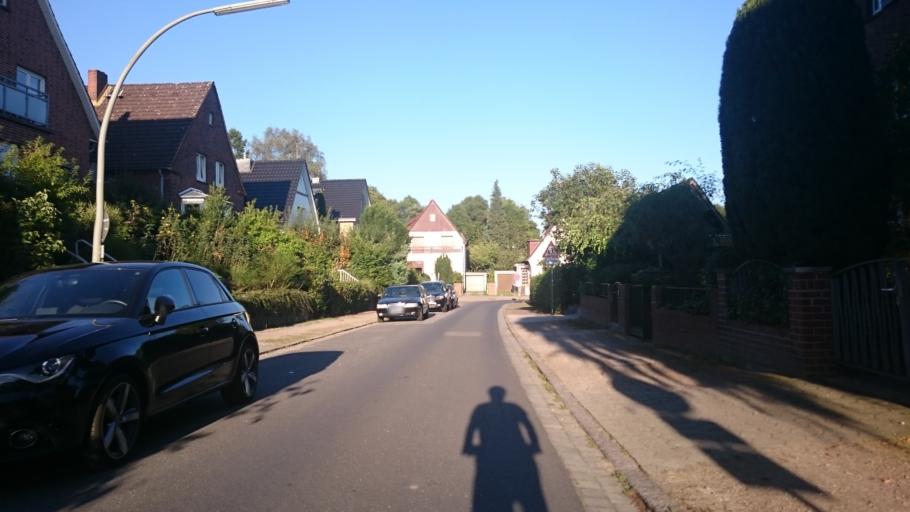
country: DE
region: Hamburg
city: Stellingen
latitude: 53.5704
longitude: 9.9074
